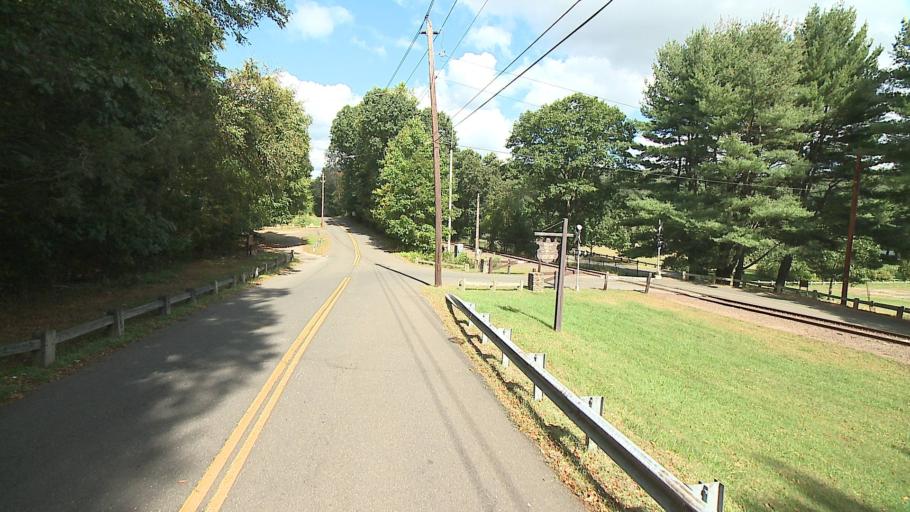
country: US
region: Connecticut
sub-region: Fairfield County
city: Shelton
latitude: 41.3428
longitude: -73.1263
